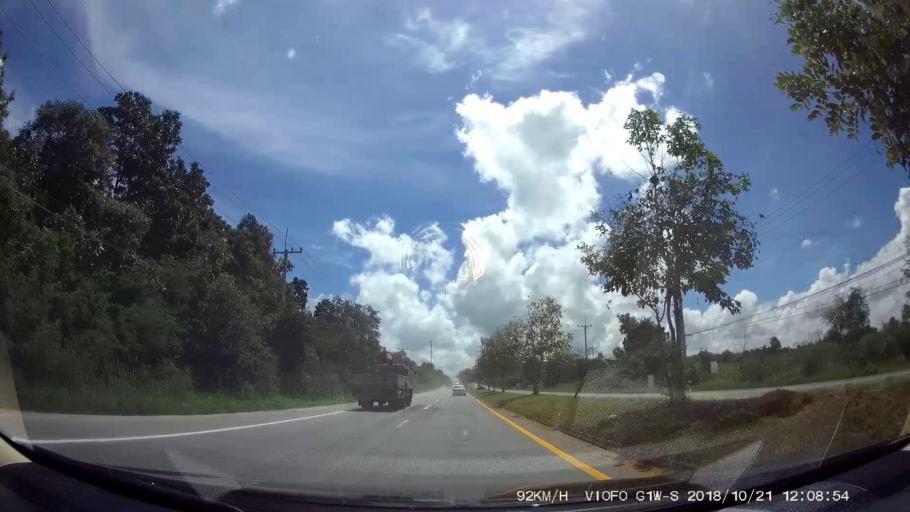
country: TH
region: Chaiyaphum
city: Chatturat
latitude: 15.4274
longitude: 101.8315
